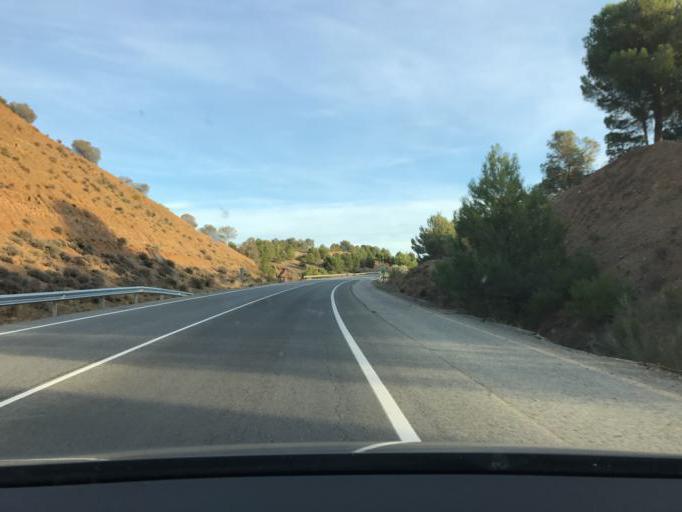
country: ES
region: Andalusia
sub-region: Provincia de Granada
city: Guadix
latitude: 37.2696
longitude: -3.0970
